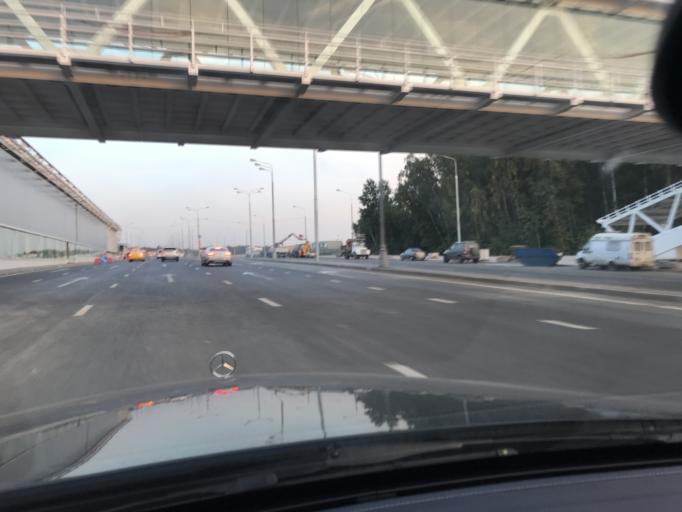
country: RU
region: Moskovskaya
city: Mosrentgen
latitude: 55.5866
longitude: 37.4323
